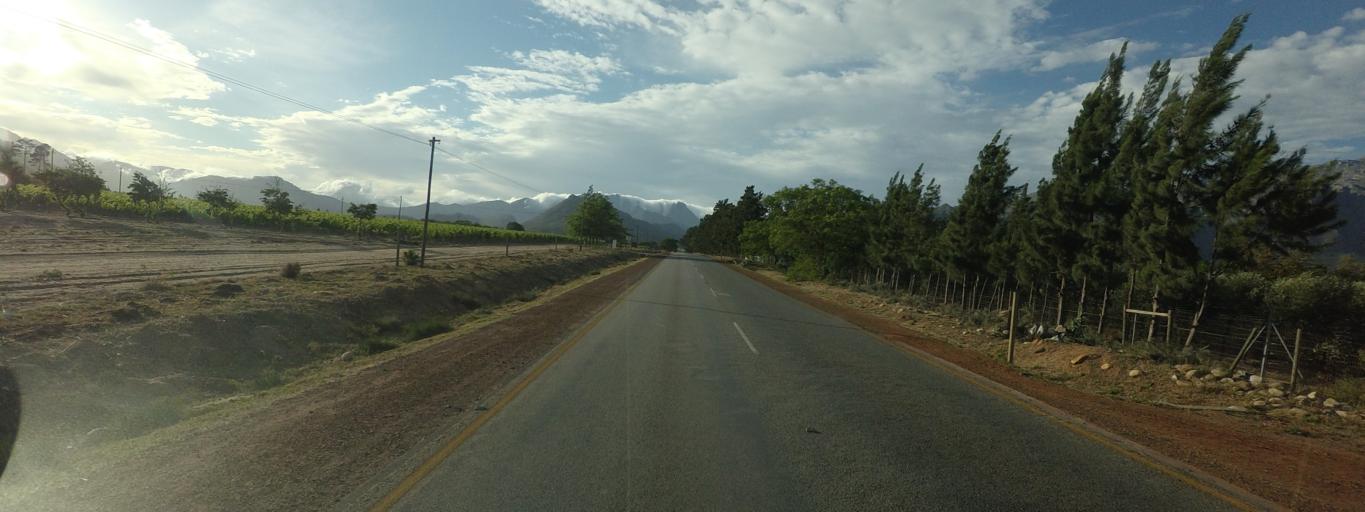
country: ZA
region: Western Cape
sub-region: Cape Winelands District Municipality
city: Paarl
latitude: -33.8654
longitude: 19.0407
